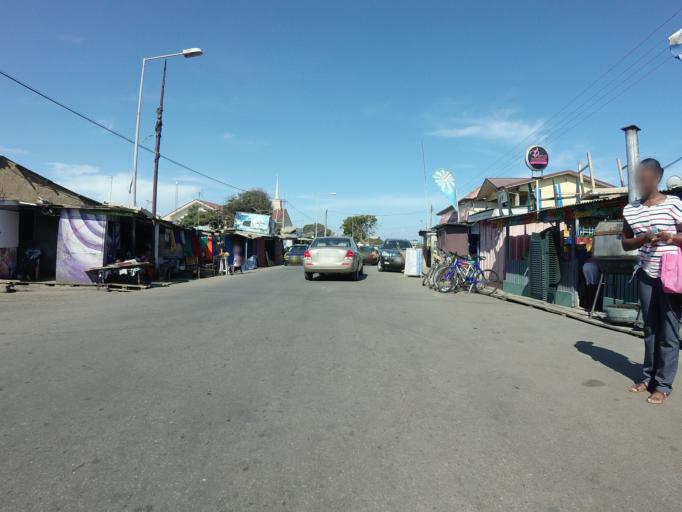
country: GH
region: Greater Accra
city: Accra
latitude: 5.5612
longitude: -0.1539
